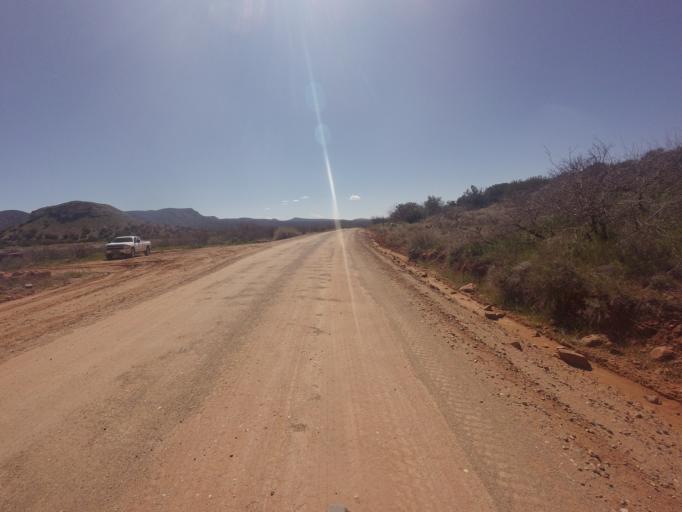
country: US
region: Arizona
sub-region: Yavapai County
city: Lake Montezuma
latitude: 34.6615
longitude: -111.7133
